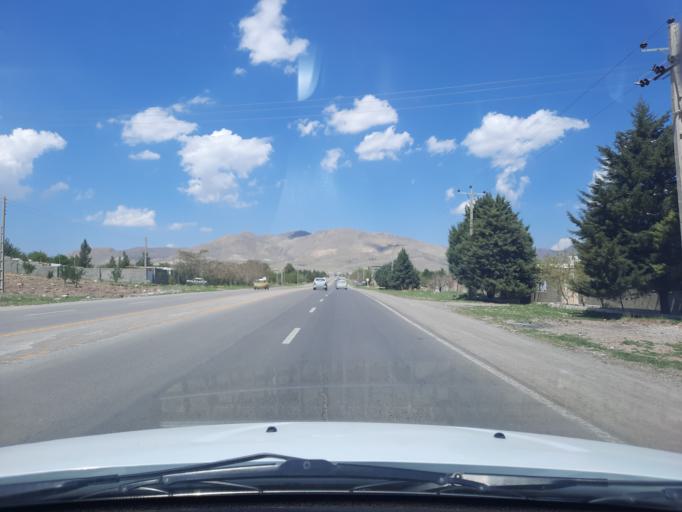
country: IR
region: Qazvin
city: Alvand
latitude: 36.3134
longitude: 50.1457
